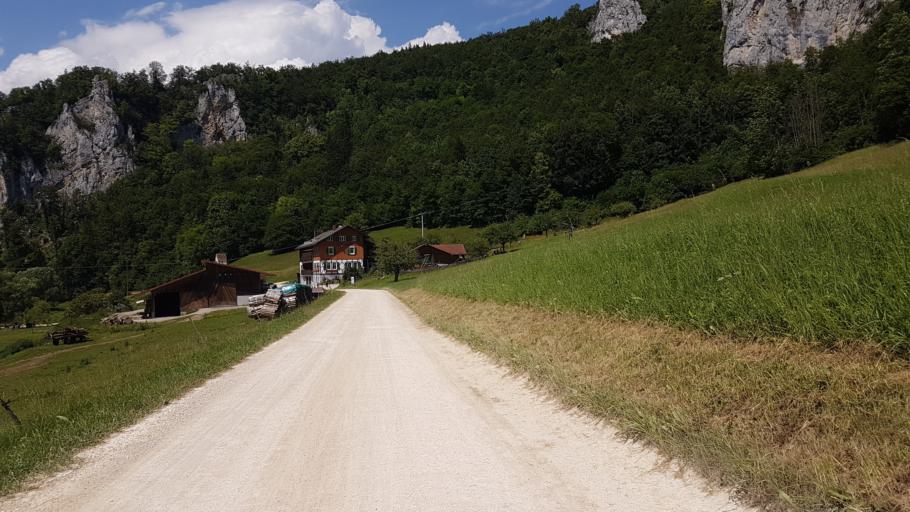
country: DE
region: Baden-Wuerttemberg
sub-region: Tuebingen Region
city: Beuron
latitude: 48.0284
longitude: 8.9641
